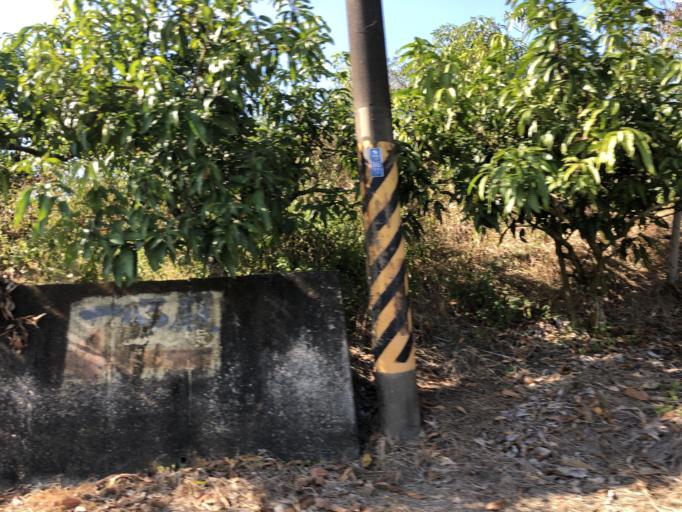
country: TW
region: Taiwan
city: Yujing
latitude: 23.0335
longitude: 120.3950
